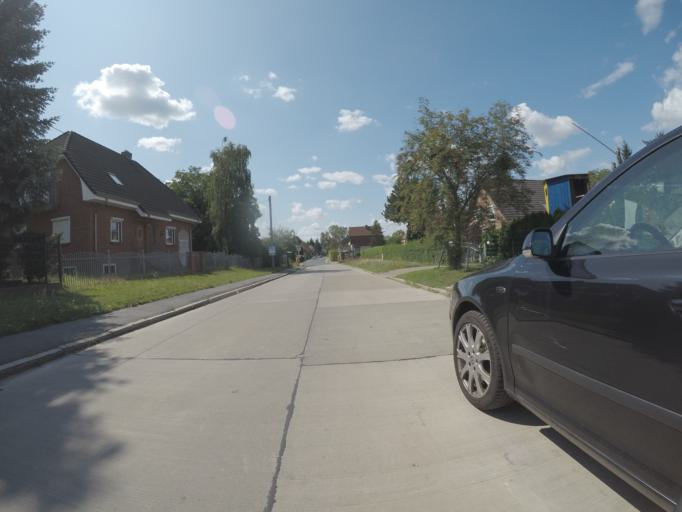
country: DE
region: Berlin
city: Mahlsdorf
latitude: 52.5095
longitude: 13.6068
